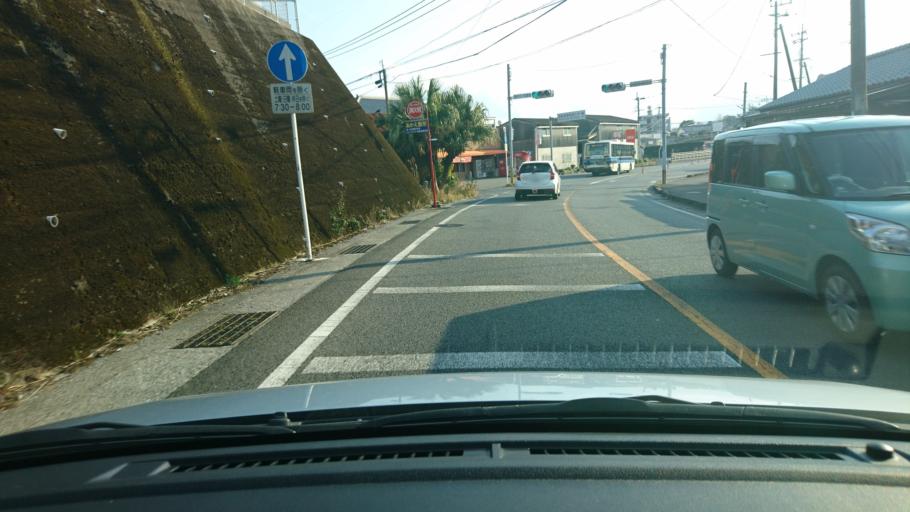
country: JP
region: Miyazaki
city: Miyazaki-shi
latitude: 31.8847
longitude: 131.4090
